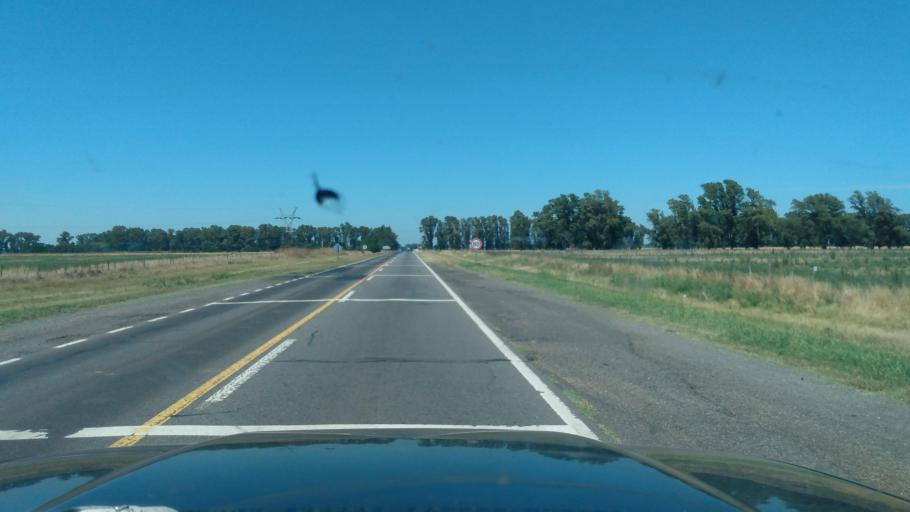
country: AR
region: Buenos Aires
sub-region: Partido de Bragado
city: Bragado
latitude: -35.0923
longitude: -60.3946
